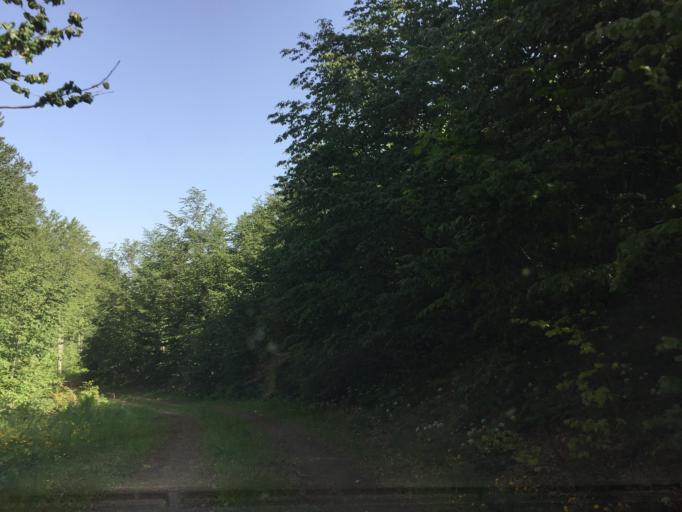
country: HR
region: Primorsko-Goranska
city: Podhum
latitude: 45.4270
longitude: 14.5822
